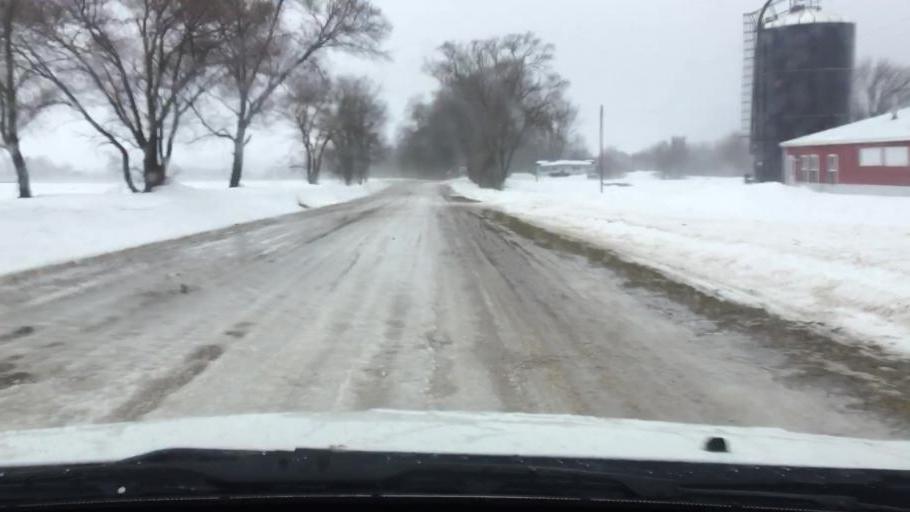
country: US
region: Michigan
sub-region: Charlevoix County
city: East Jordan
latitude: 45.1308
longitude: -85.1597
